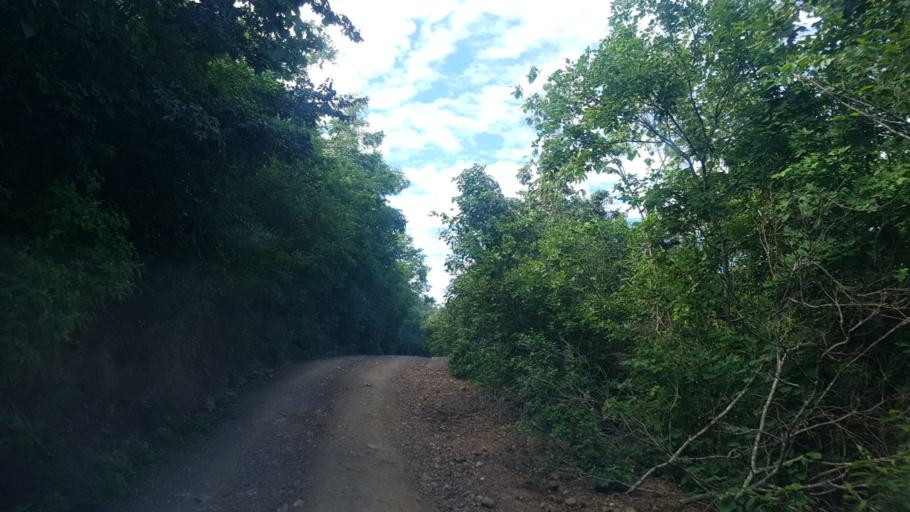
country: NI
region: Nueva Segovia
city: Ocotal
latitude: 13.5997
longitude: -86.4423
